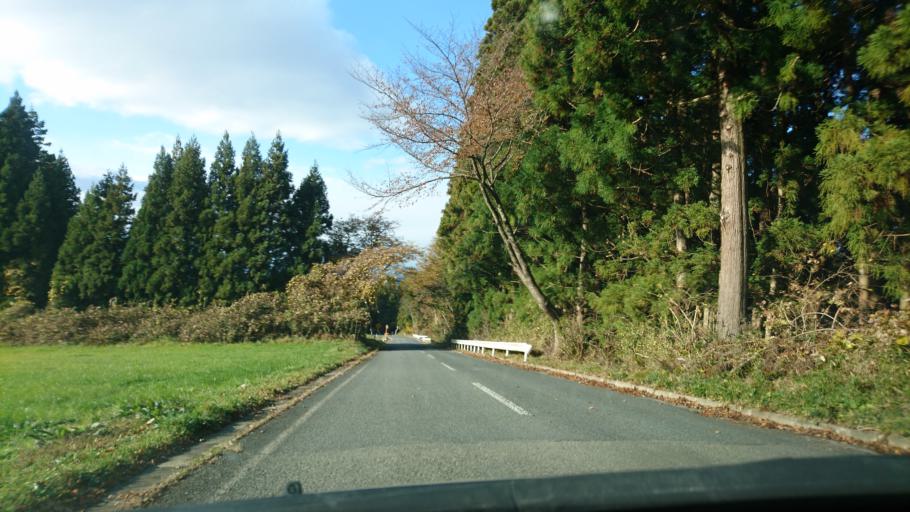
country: JP
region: Iwate
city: Mizusawa
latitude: 39.0309
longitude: 141.1615
